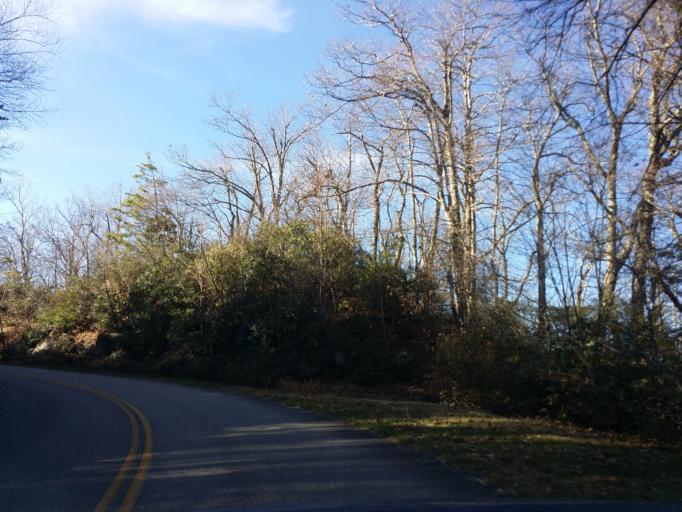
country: US
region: North Carolina
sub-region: Buncombe County
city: Black Mountain
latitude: 35.7389
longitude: -82.1959
